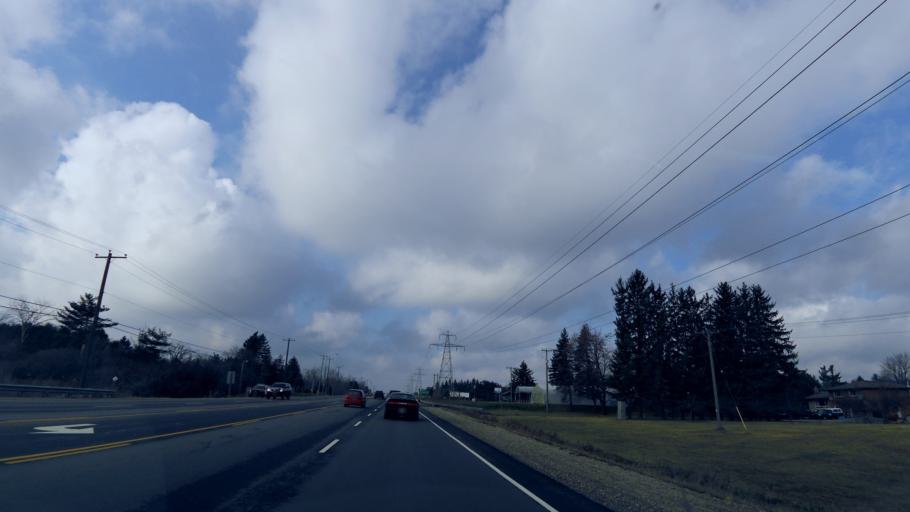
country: CA
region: Ontario
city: Ancaster
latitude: 43.3805
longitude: -80.0107
